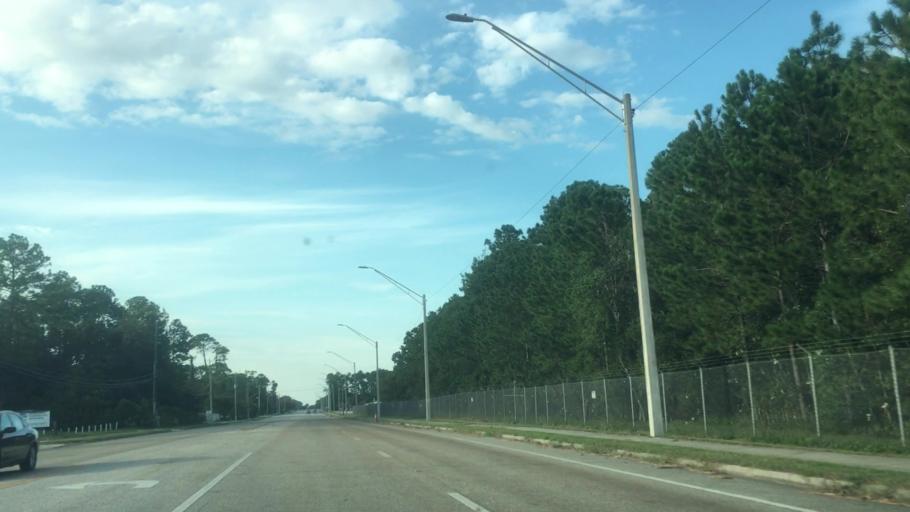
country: US
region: Florida
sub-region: Duval County
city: Atlantic Beach
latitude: 30.3273
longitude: -81.5231
